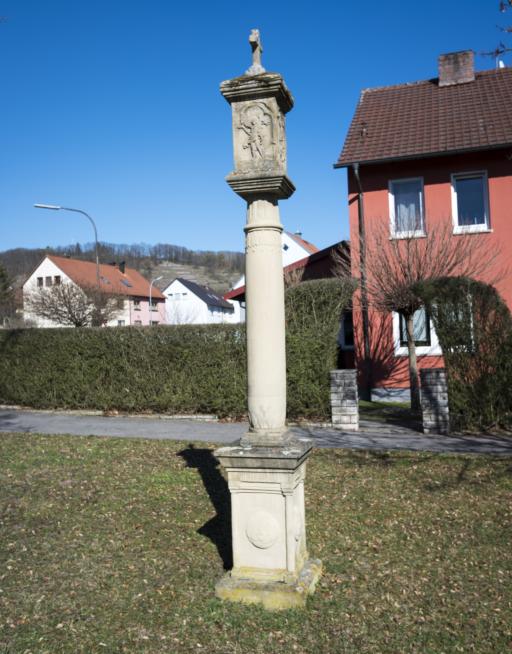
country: DE
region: Bavaria
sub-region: Regierungsbezirk Unterfranken
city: Zeil
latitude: 50.0130
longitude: 10.5936
